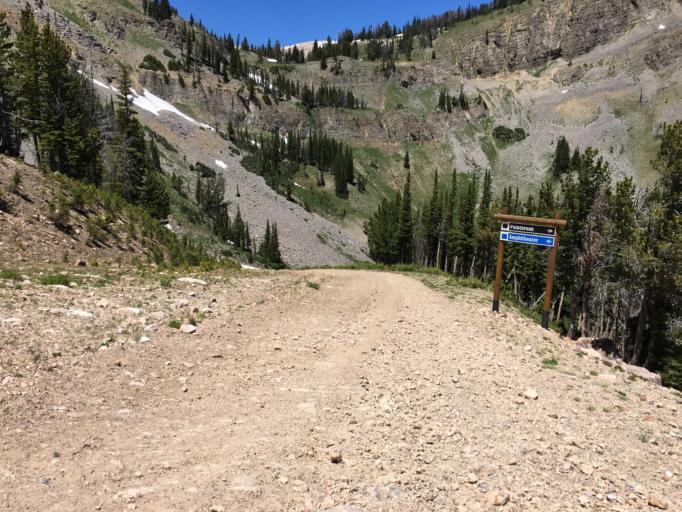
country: US
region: Wyoming
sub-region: Teton County
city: Moose Wilson Road
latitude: 43.5957
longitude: -110.8593
